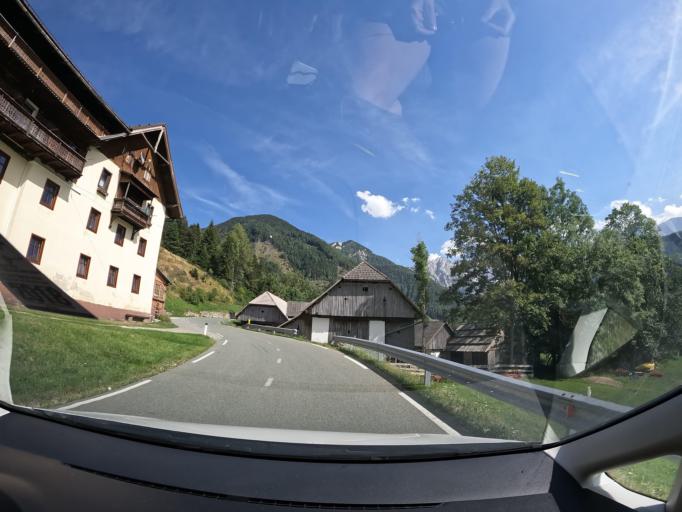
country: AT
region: Carinthia
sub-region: Politischer Bezirk Feldkirchen
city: Glanegg
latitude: 46.7398
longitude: 14.1831
